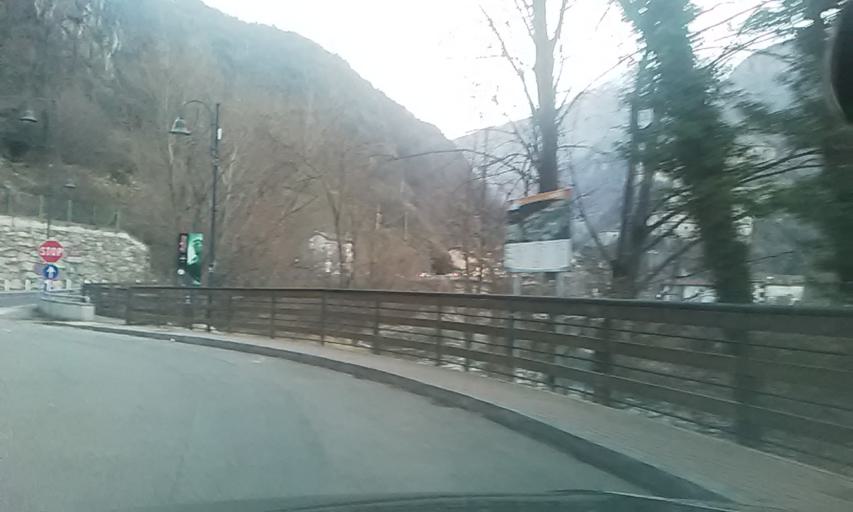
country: IT
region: Aosta Valley
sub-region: Valle d'Aosta
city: Hone
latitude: 45.6144
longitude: 7.7431
